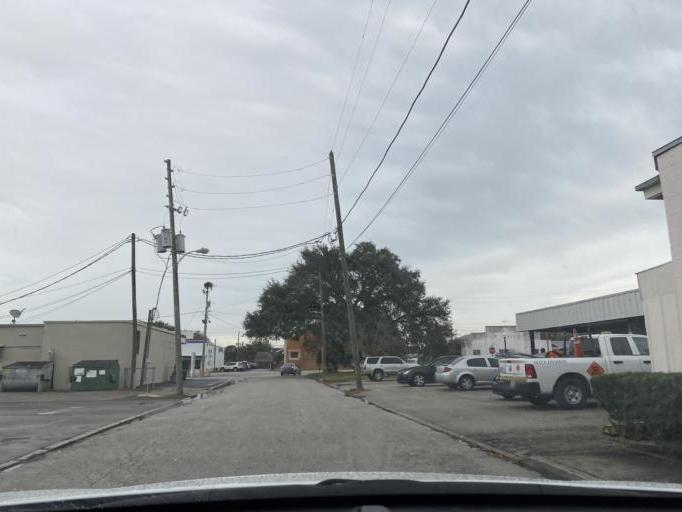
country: US
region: Florida
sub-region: Orange County
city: Winter Garden
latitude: 28.5650
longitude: -81.5844
